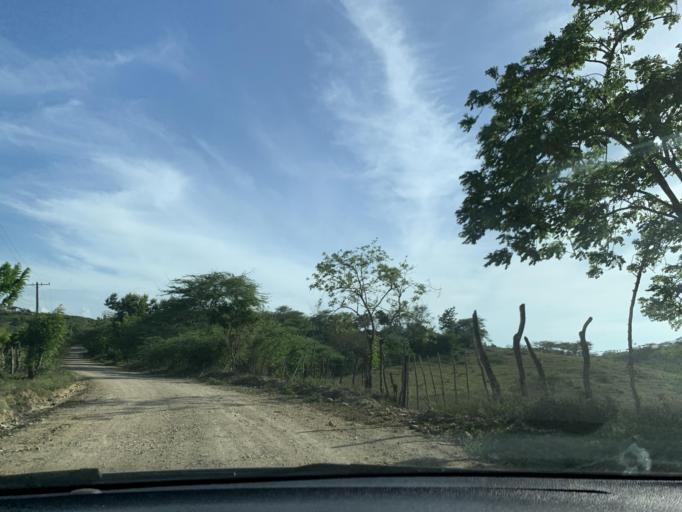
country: DO
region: Puerto Plata
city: Luperon
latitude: 19.8788
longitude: -70.9325
